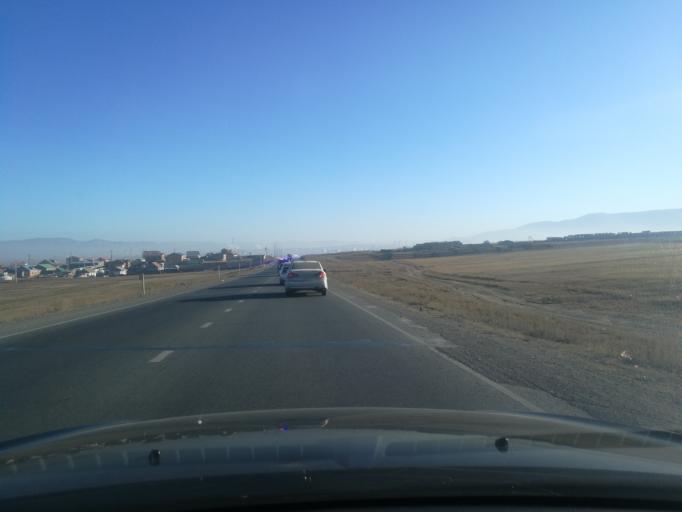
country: MN
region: Ulaanbaatar
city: Ulaanbaatar
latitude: 47.8413
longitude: 106.7234
